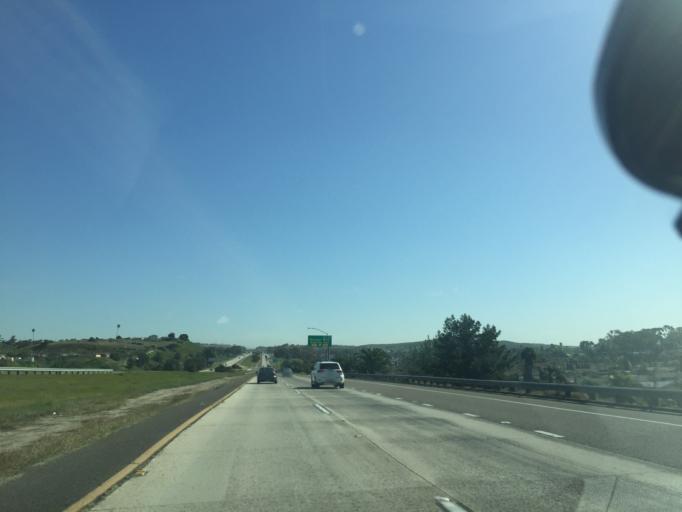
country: US
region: California
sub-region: San Diego County
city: Imperial Beach
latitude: 32.5682
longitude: -117.0578
